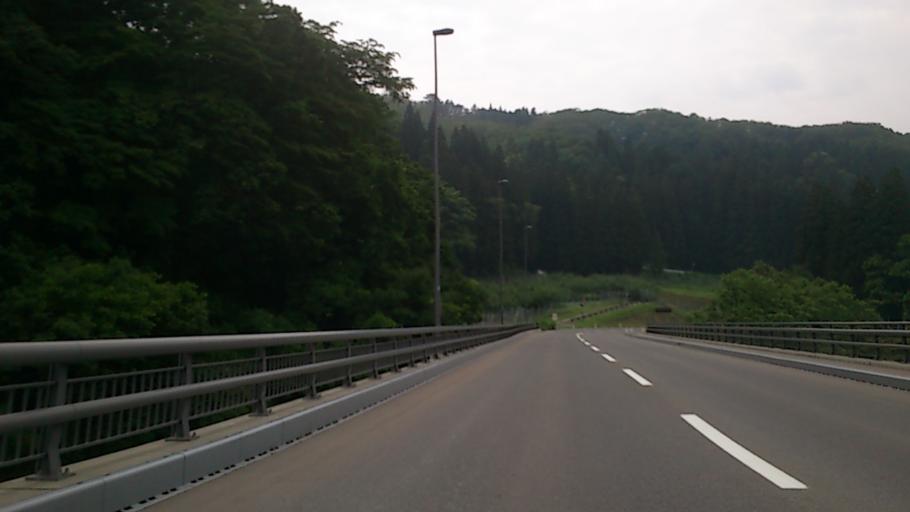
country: JP
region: Aomori
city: Hirosaki
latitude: 40.5745
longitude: 140.2993
